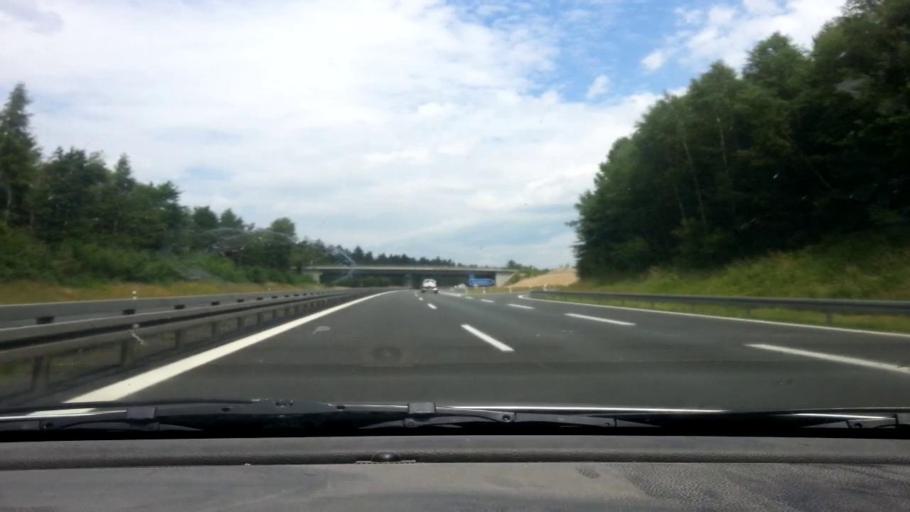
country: DE
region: Bavaria
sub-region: Upper Palatinate
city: Wiesau
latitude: 49.9094
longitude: 12.2203
